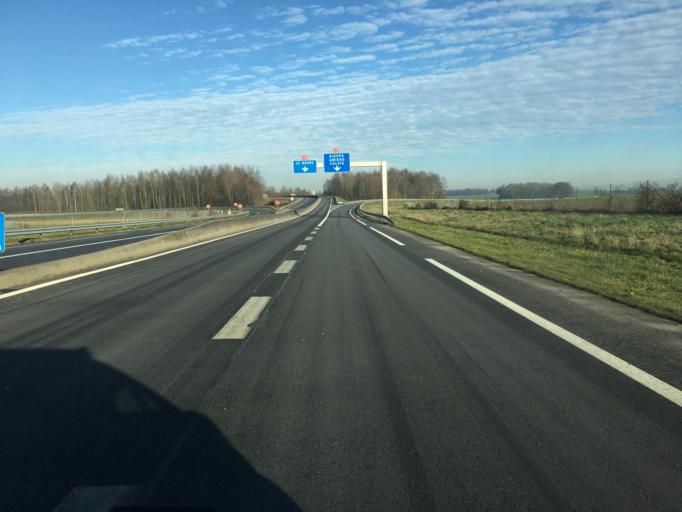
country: FR
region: Haute-Normandie
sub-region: Departement de la Seine-Maritime
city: Yerville
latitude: 49.6490
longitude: 0.8438
